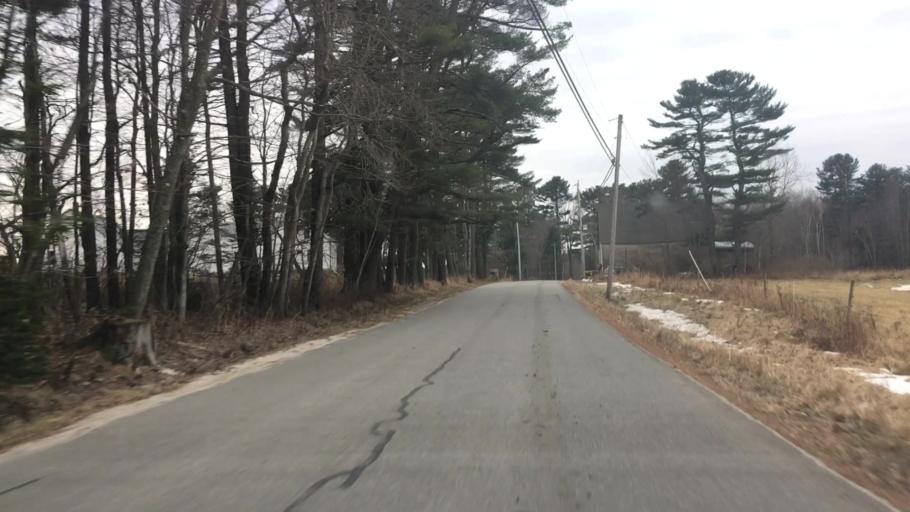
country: US
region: Maine
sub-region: Cumberland County
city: Freeport
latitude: 43.8323
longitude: -70.0805
